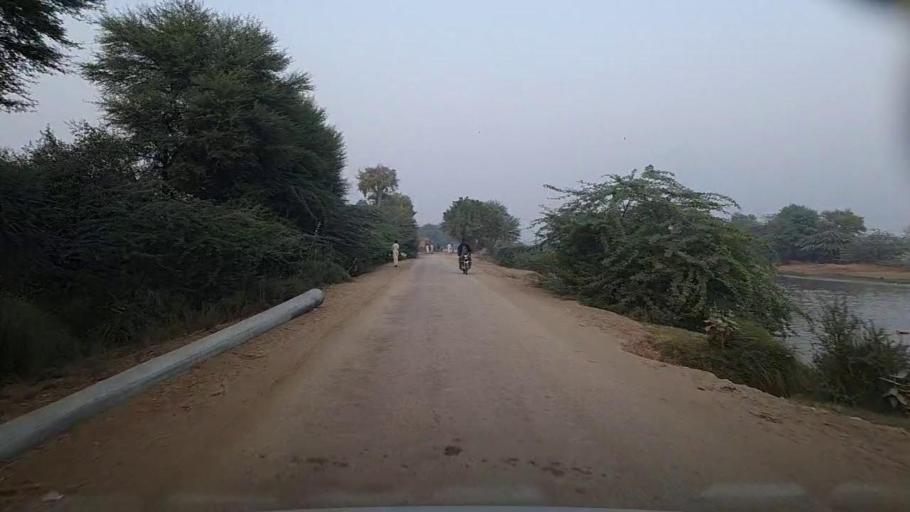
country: PK
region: Sindh
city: Bozdar
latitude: 27.0490
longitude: 68.5954
